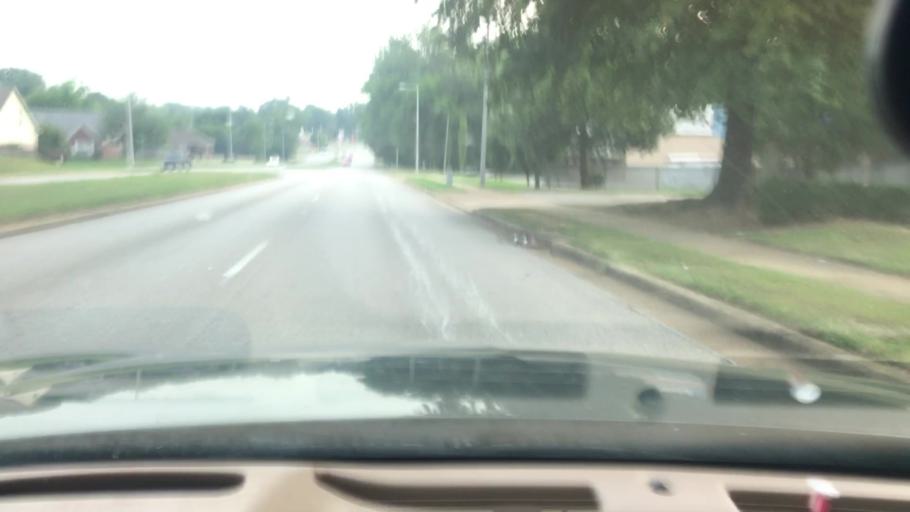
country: US
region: Tennessee
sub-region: Shelby County
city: Bartlett
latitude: 35.1795
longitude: -89.8714
